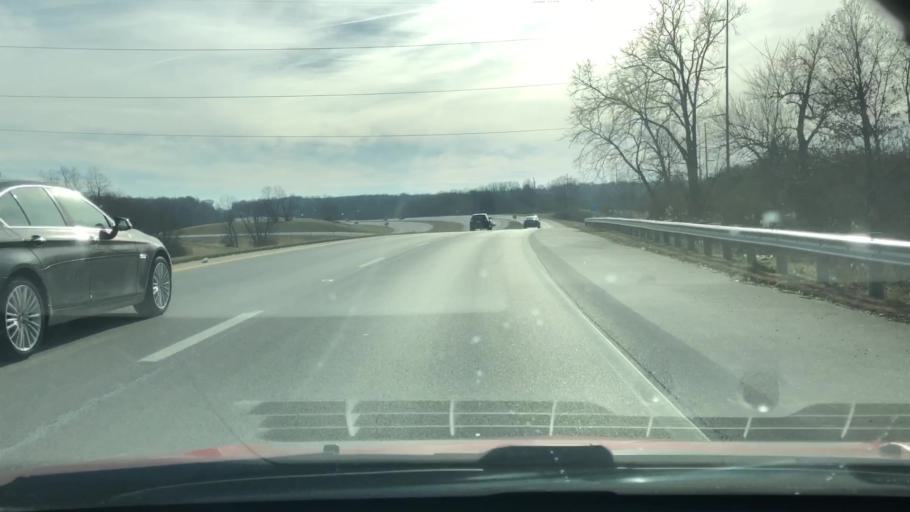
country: US
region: Ohio
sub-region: Montgomery County
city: Riverside
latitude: 39.7695
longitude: -84.0910
